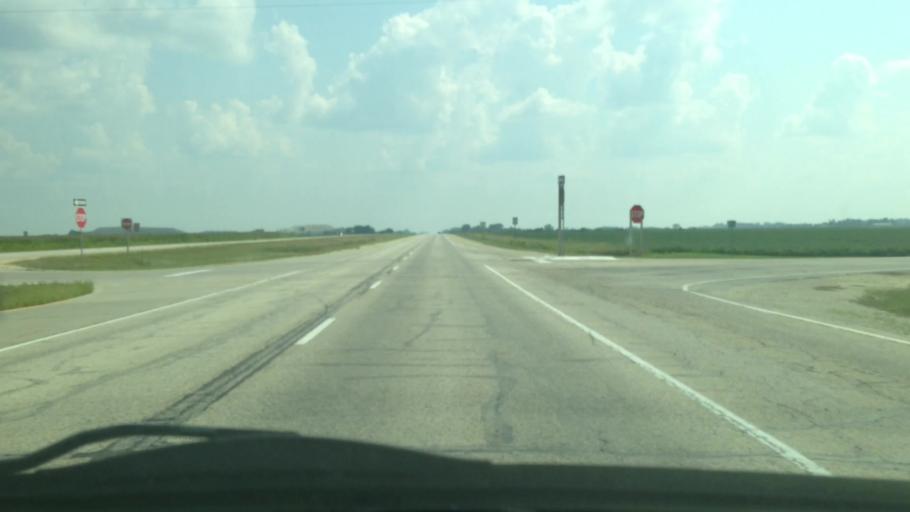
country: US
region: Iowa
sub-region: Bremer County
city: Tripoli
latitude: 42.8481
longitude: -92.3375
